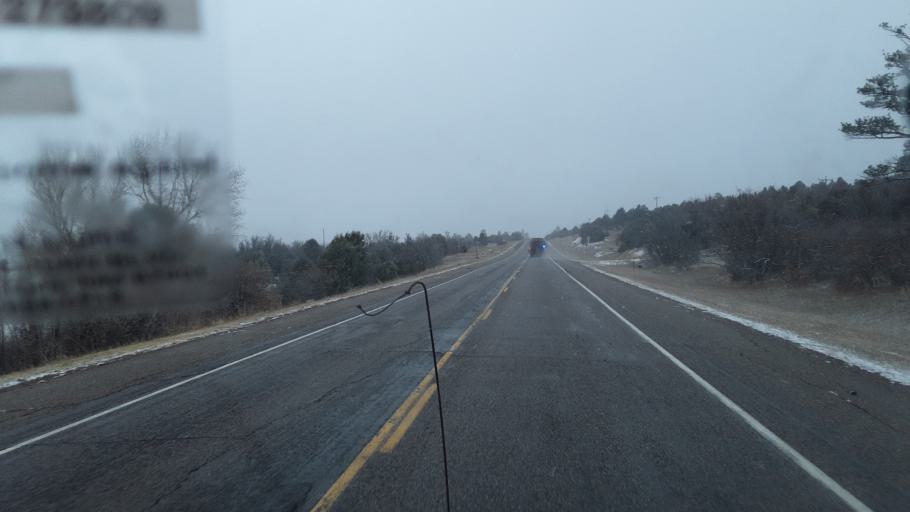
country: US
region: New Mexico
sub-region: Rio Arriba County
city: Tierra Amarilla
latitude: 36.7954
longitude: -106.5628
